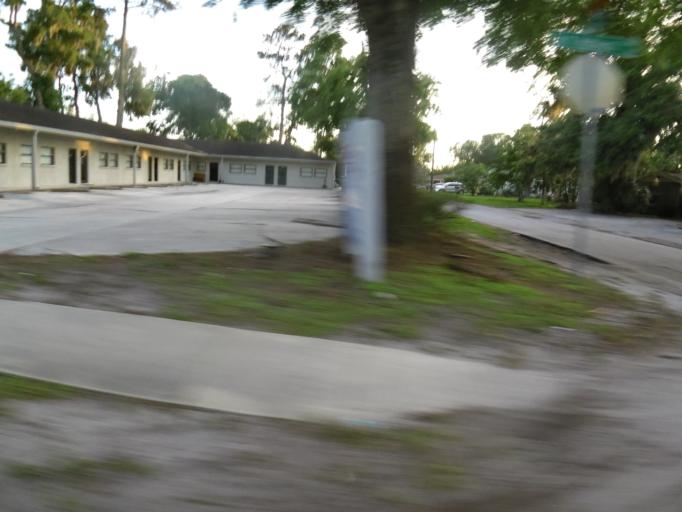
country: US
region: Florida
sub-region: Duval County
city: Jacksonville
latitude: 30.3030
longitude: -81.6161
